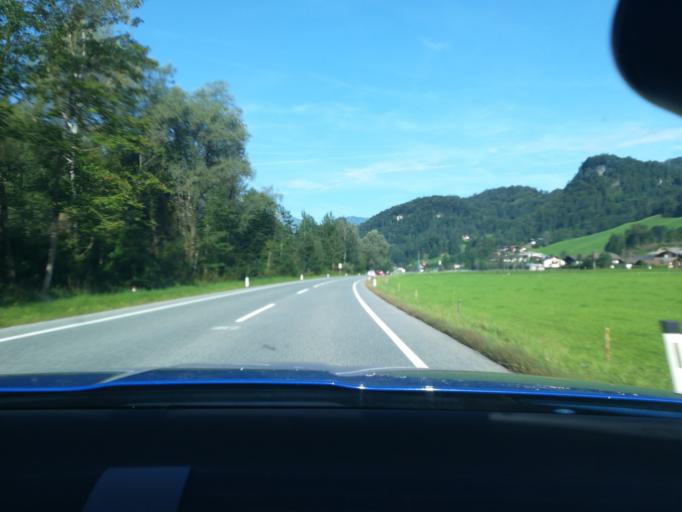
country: AT
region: Salzburg
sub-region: Politischer Bezirk Hallein
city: Scheffau am Tennengebirge
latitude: 47.5872
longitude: 13.2145
